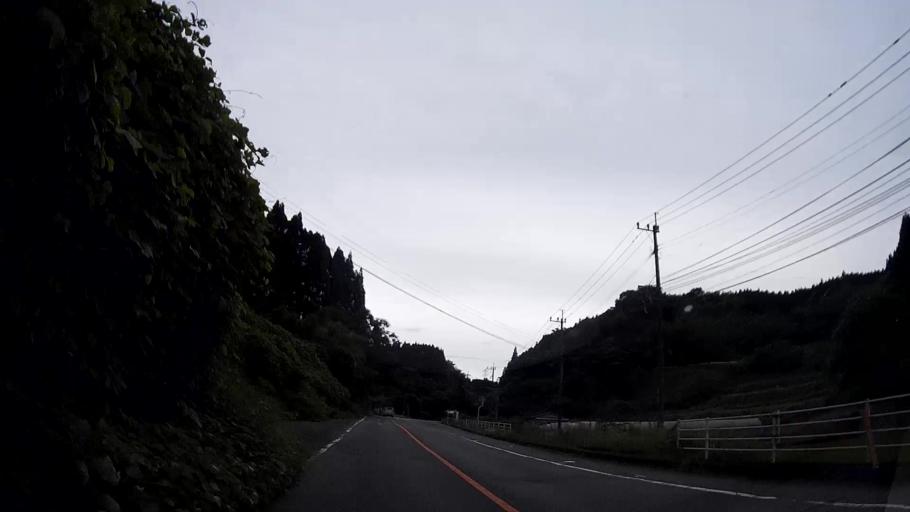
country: JP
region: Kumamoto
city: Kikuchi
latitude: 33.0149
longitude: 130.8808
